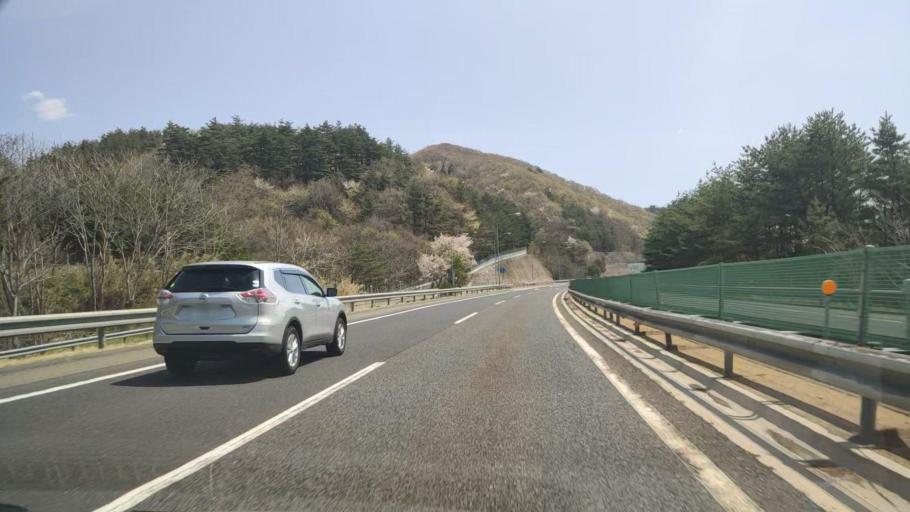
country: JP
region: Iwate
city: Ichinohe
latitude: 40.2325
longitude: 141.2970
